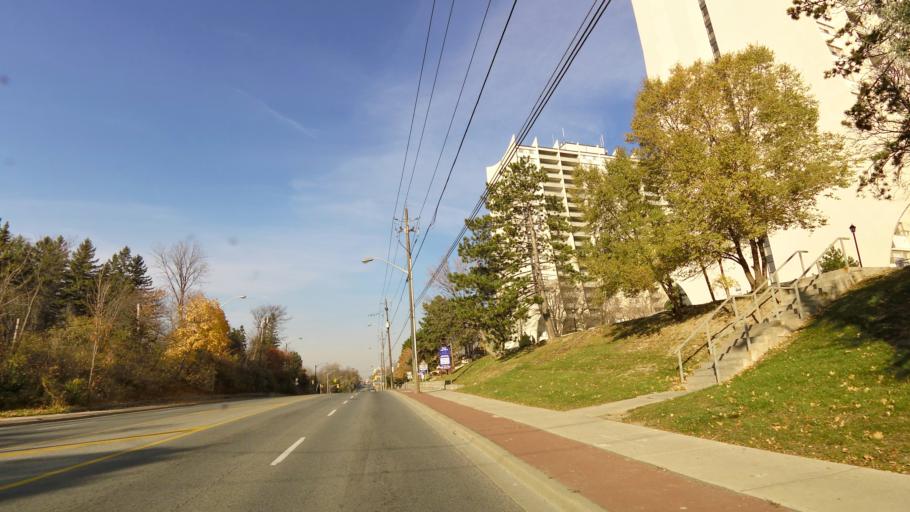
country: CA
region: Ontario
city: Concord
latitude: 43.7302
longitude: -79.5108
